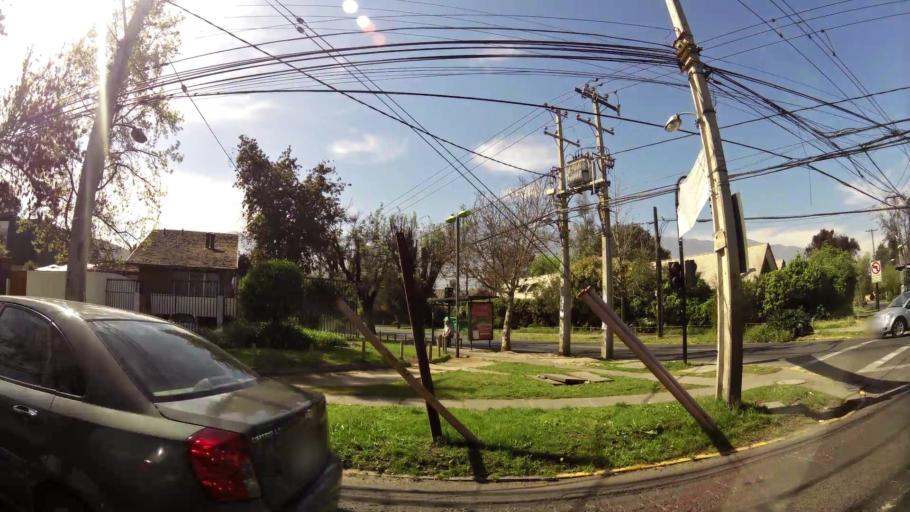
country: CL
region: Santiago Metropolitan
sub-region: Provincia de Santiago
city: Villa Presidente Frei, Nunoa, Santiago, Chile
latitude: -33.4422
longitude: -70.5533
